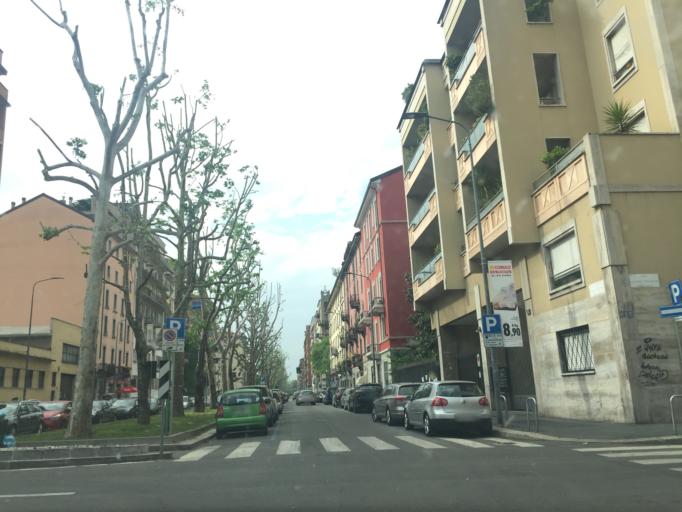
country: IT
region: Lombardy
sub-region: Citta metropolitana di Milano
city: Milano
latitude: 45.4897
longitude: 9.1671
